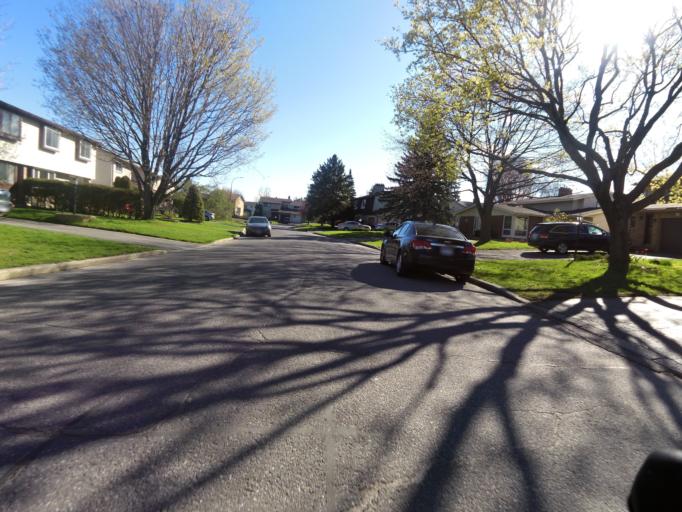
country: CA
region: Ontario
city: Bells Corners
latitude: 45.3313
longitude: -75.7469
